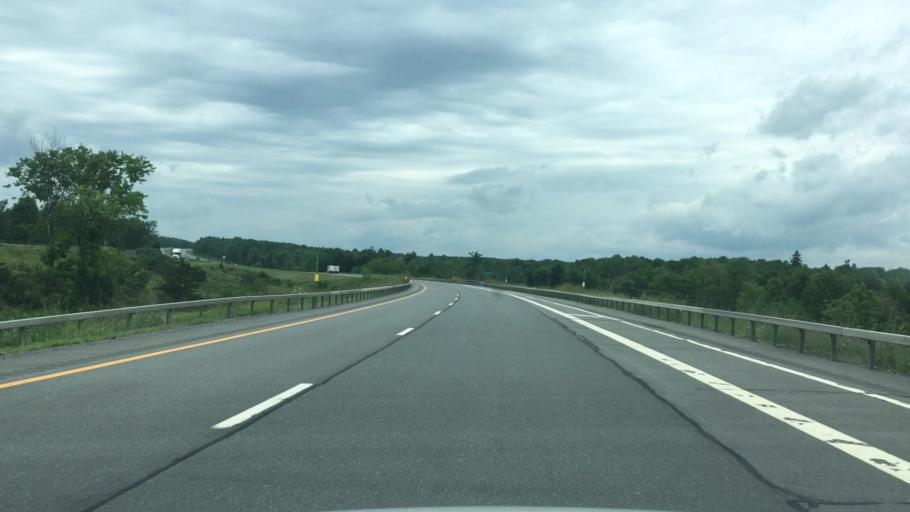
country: US
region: New York
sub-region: Schoharie County
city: Schoharie
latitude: 42.7240
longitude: -74.2393
